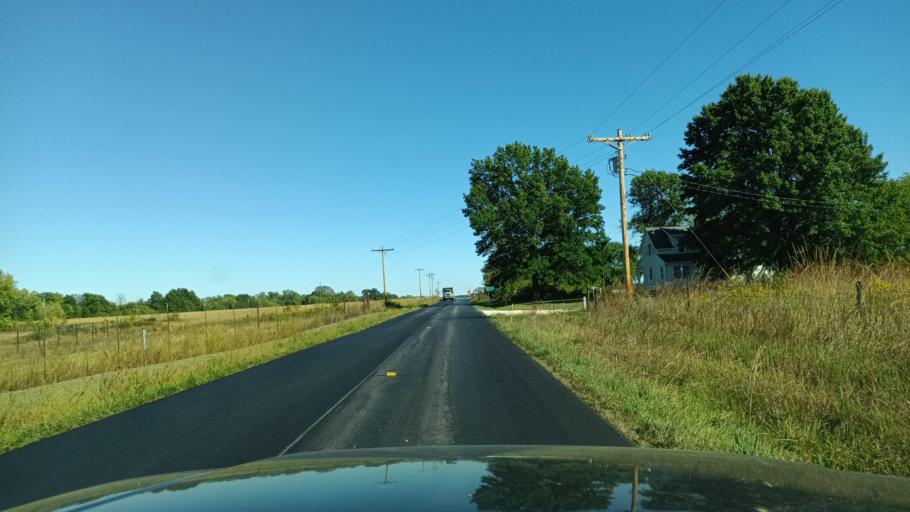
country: US
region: Missouri
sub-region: Macon County
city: La Plata
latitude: 39.9281
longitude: -92.5725
